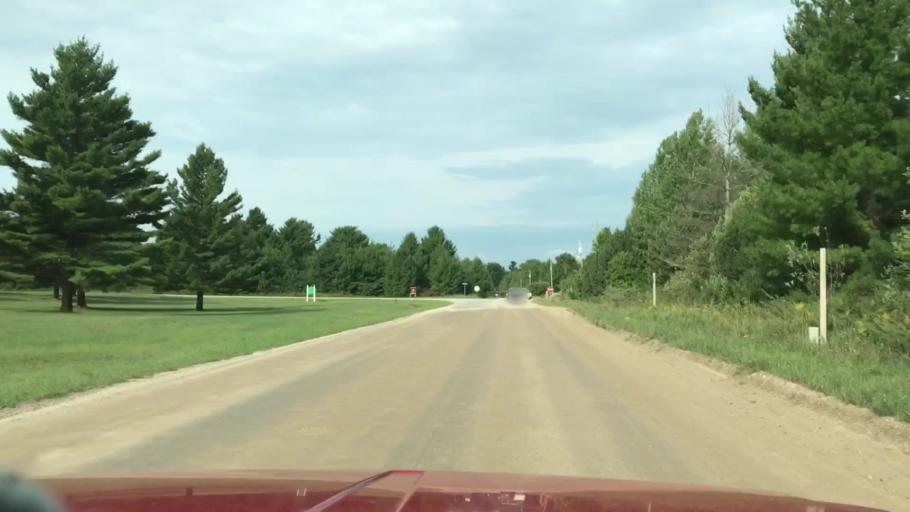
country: US
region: Michigan
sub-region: Charlevoix County
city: Charlevoix
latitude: 45.7286
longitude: -85.5245
